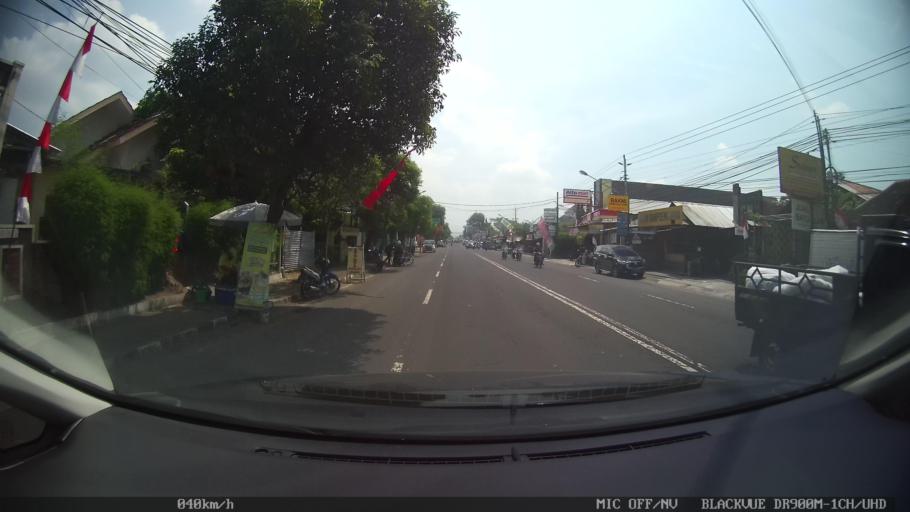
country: ID
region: Daerah Istimewa Yogyakarta
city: Yogyakarta
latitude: -7.8133
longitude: 110.4021
